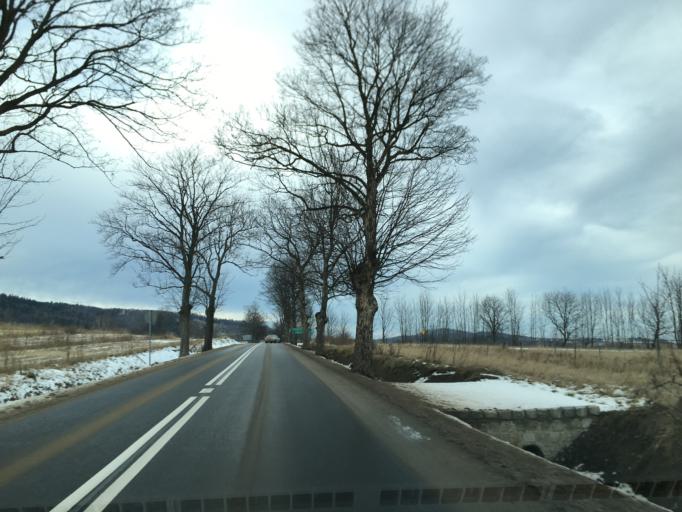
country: PL
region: Lower Silesian Voivodeship
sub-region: Powiat walbrzyski
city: Jedlina-Zdroj
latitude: 50.7410
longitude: 16.3454
